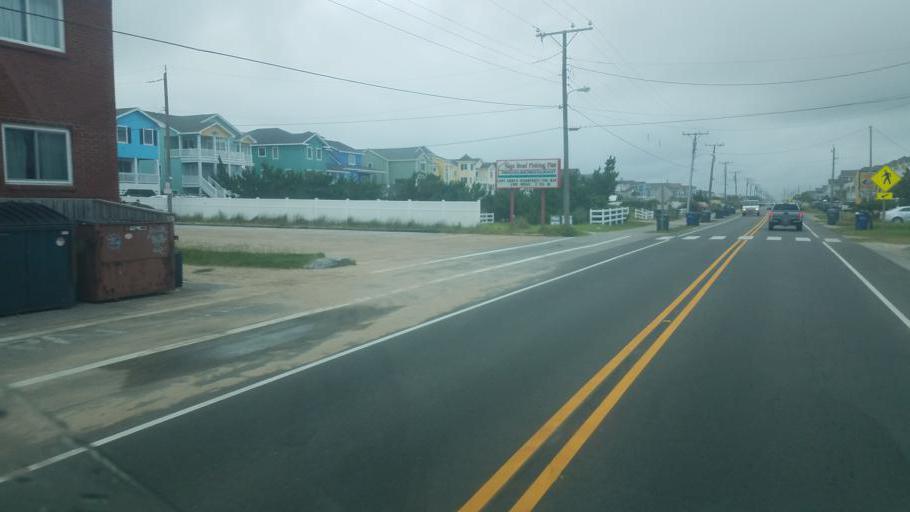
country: US
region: North Carolina
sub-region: Dare County
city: Nags Head
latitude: 35.9729
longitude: -75.6330
